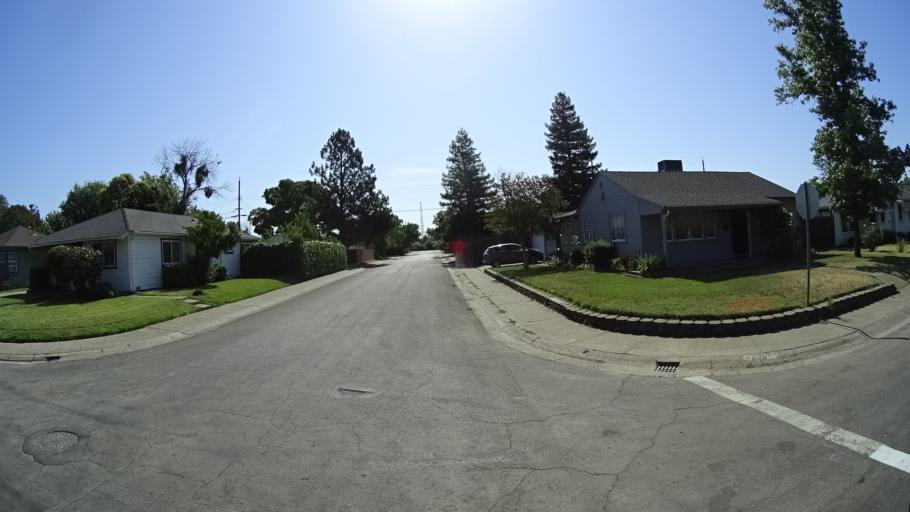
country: US
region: California
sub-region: Sacramento County
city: Florin
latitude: 38.5449
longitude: -121.4304
